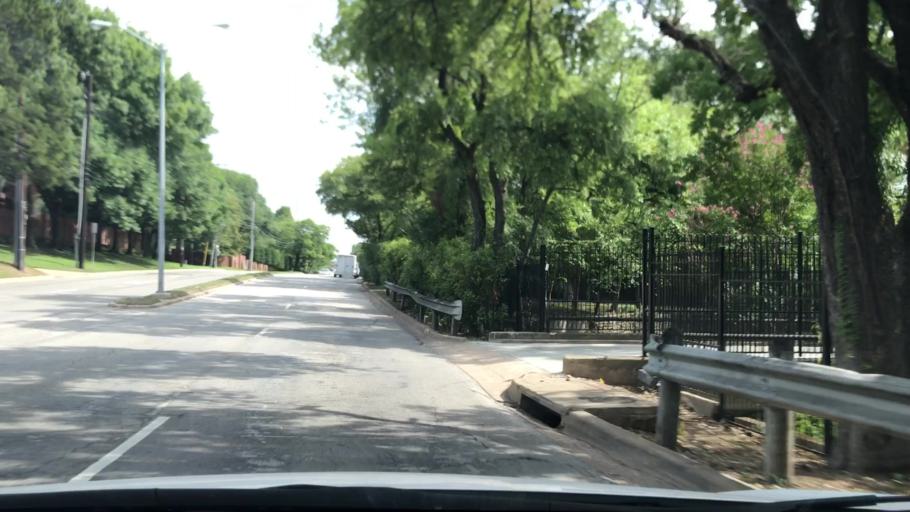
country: US
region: Texas
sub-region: Dallas County
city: University Park
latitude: 32.8778
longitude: -96.8212
